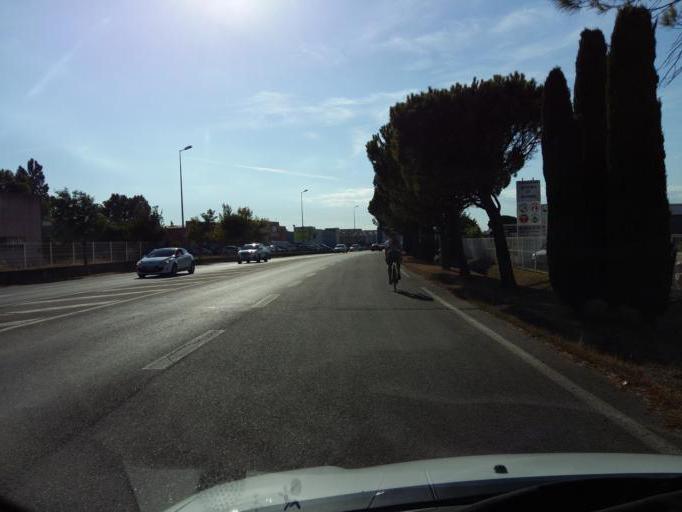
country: FR
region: Provence-Alpes-Cote d'Azur
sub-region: Departement du Vaucluse
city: Le Thor
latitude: 43.9221
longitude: 5.0159
